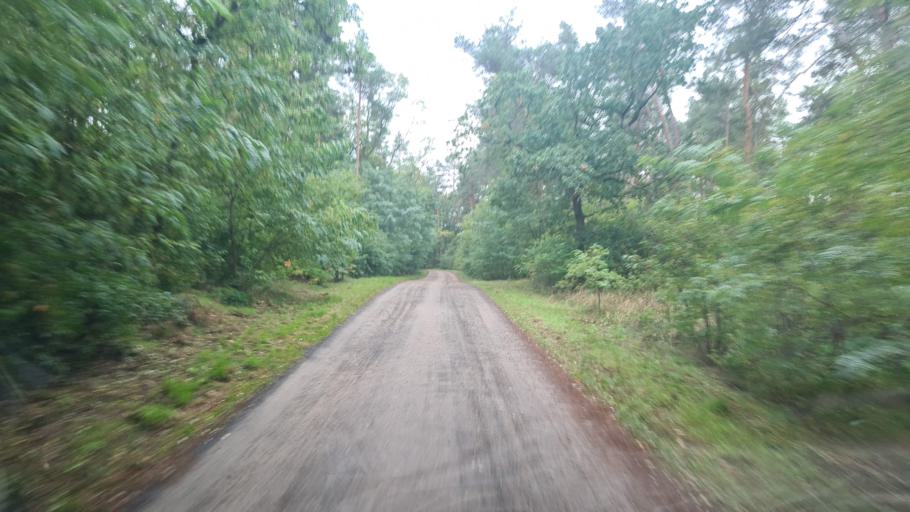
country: DE
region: Brandenburg
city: Storkow
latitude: 52.2299
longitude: 13.9333
